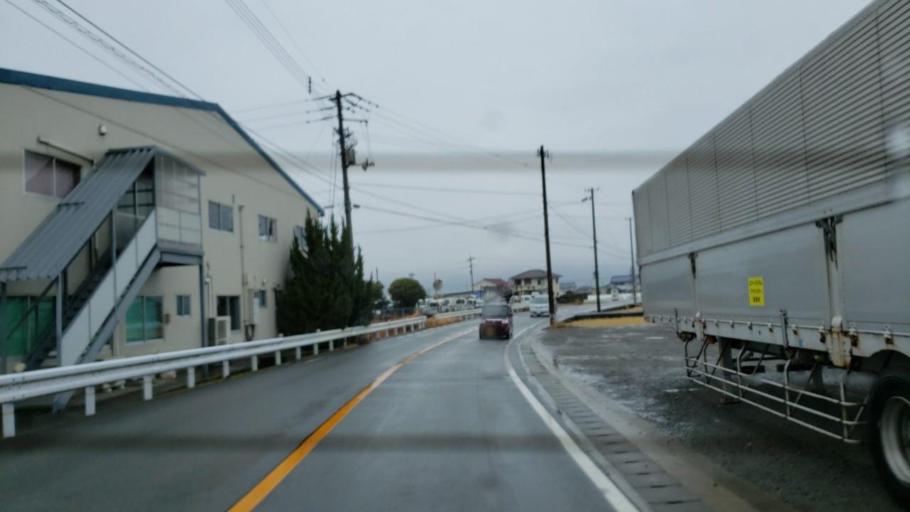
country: JP
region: Tokushima
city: Ishii
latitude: 34.0981
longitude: 134.4078
